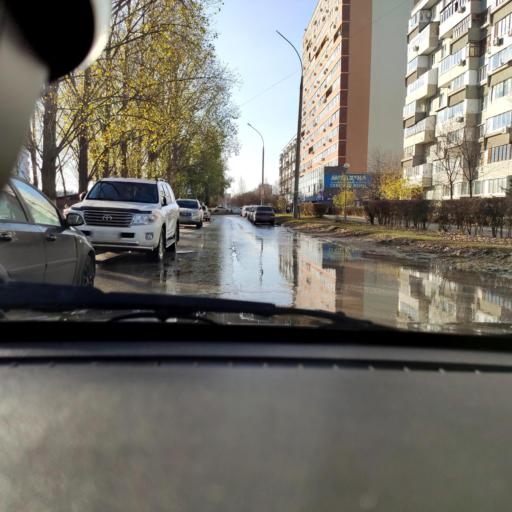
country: RU
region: Samara
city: Tol'yatti
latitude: 53.5351
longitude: 49.3435
